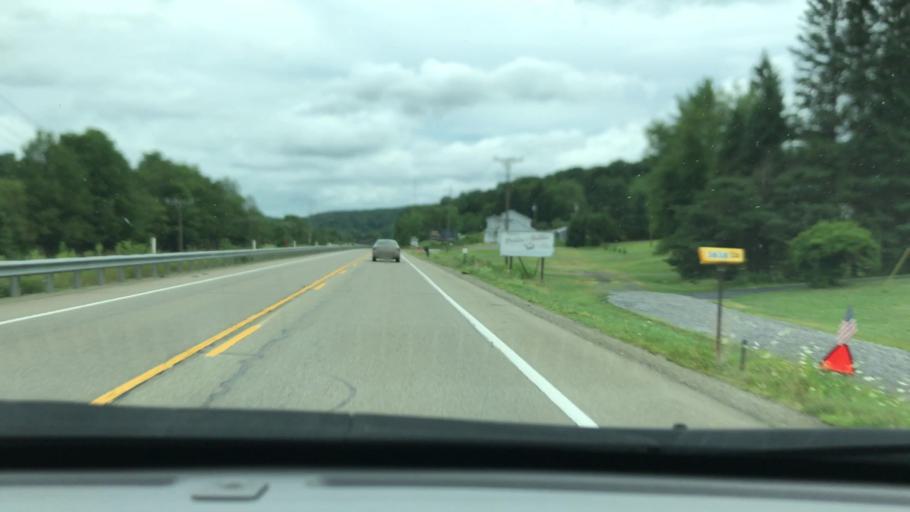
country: US
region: Pennsylvania
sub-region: Elk County
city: Johnsonburg
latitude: 41.5430
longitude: -78.6812
